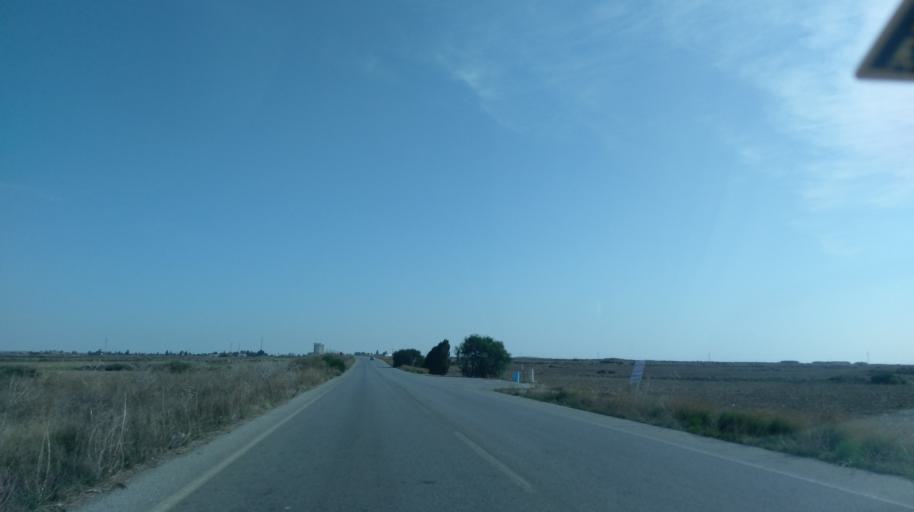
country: CY
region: Ammochostos
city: Lefkonoiko
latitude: 35.2565
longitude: 33.7023
